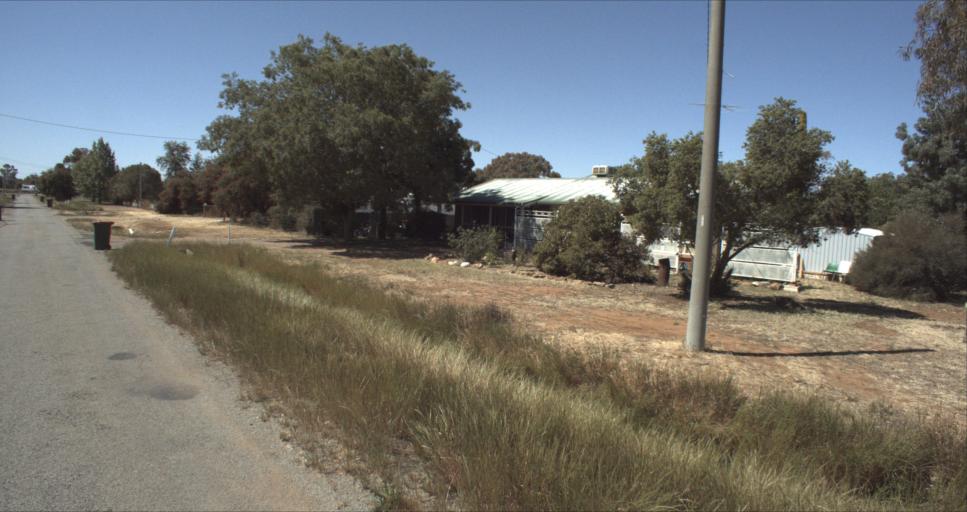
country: AU
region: New South Wales
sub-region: Leeton
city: Leeton
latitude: -34.5546
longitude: 146.3832
